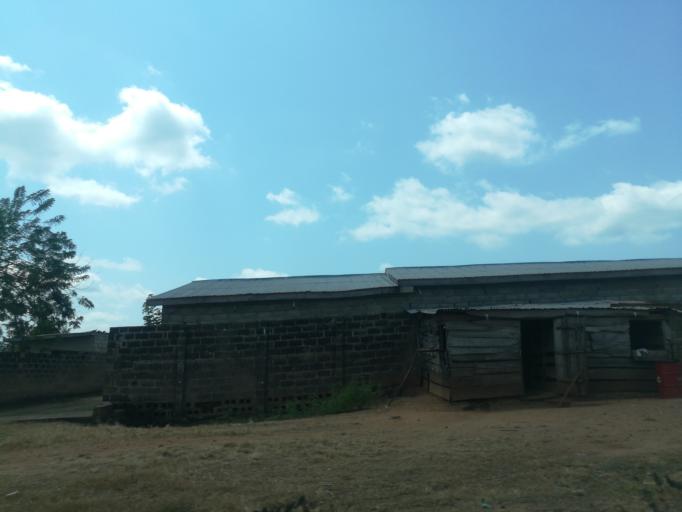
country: NG
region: Oyo
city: Moniya
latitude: 7.5610
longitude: 3.9096
